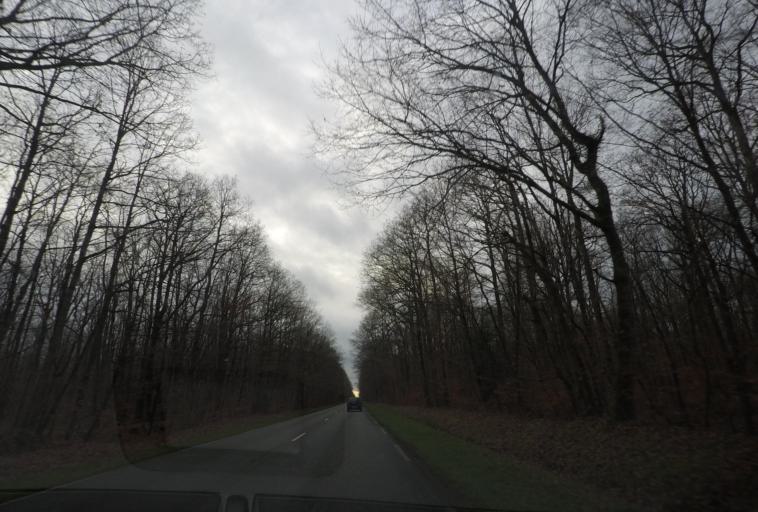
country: FR
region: Pays de la Loire
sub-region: Departement de la Sarthe
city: Vibraye
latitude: 48.0349
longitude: 0.7459
